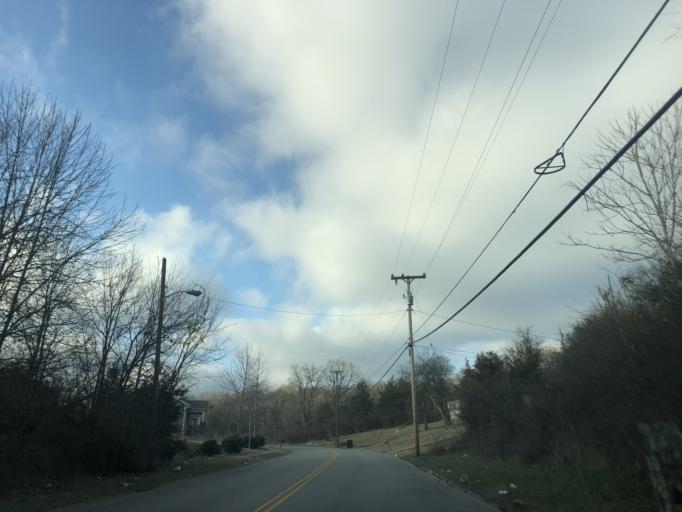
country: US
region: Tennessee
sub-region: Davidson County
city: Nashville
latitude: 36.2097
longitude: -86.7843
